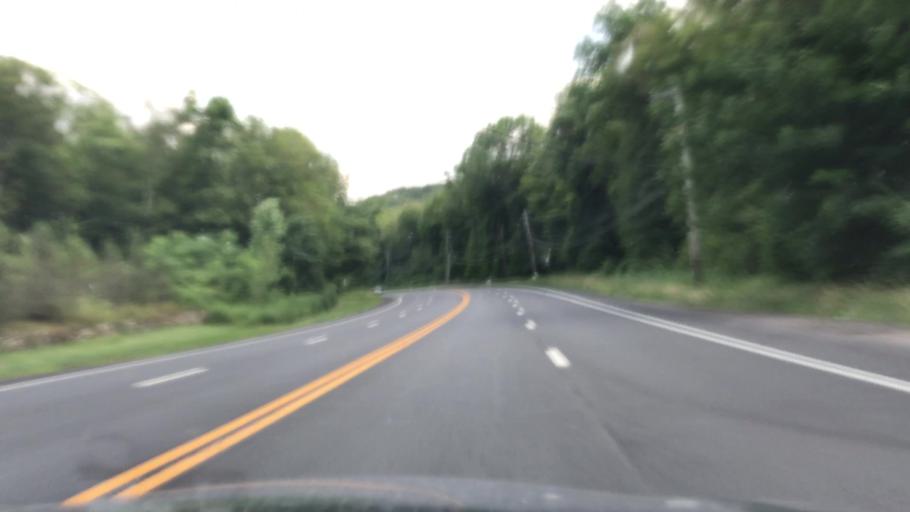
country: US
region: New York
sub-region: Rockland County
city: Sloatsburg
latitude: 41.2096
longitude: -74.1852
